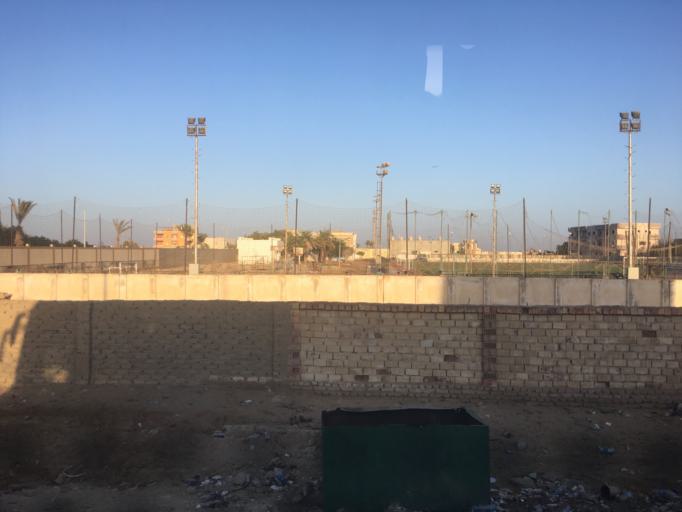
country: EG
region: Red Sea
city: Al Qusayr
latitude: 26.0959
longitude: 34.2794
